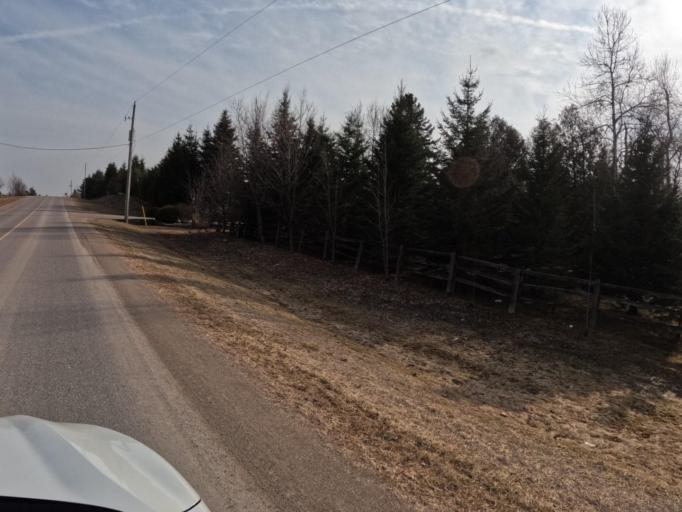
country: CA
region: Ontario
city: Orangeville
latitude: 43.8887
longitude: -80.2651
